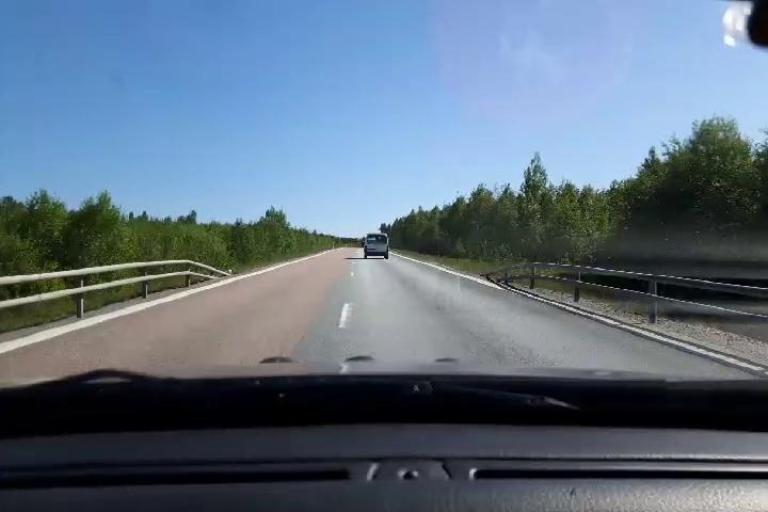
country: SE
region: Gaevleborg
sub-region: Soderhamns Kommun
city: Soderhamn
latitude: 61.4793
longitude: 16.9871
